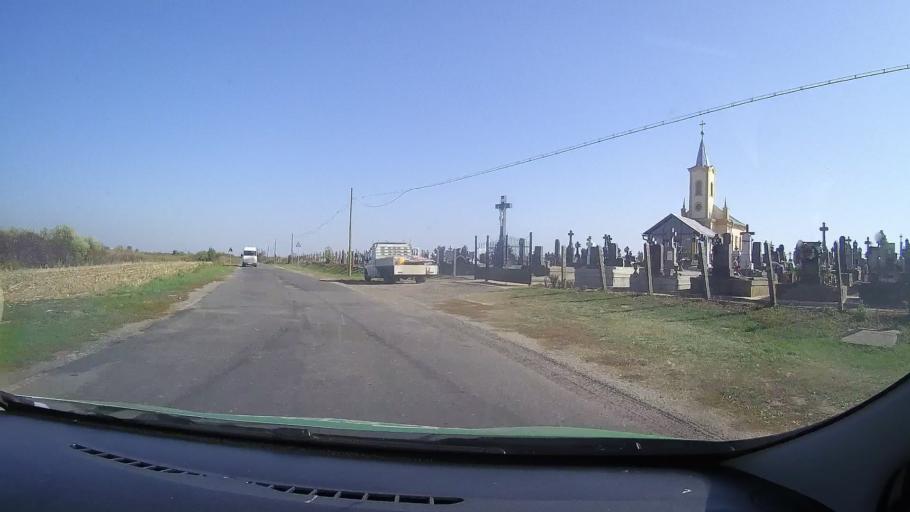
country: RO
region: Satu Mare
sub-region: Comuna Sanislau
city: Sanislau
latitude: 47.6426
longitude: 22.3346
